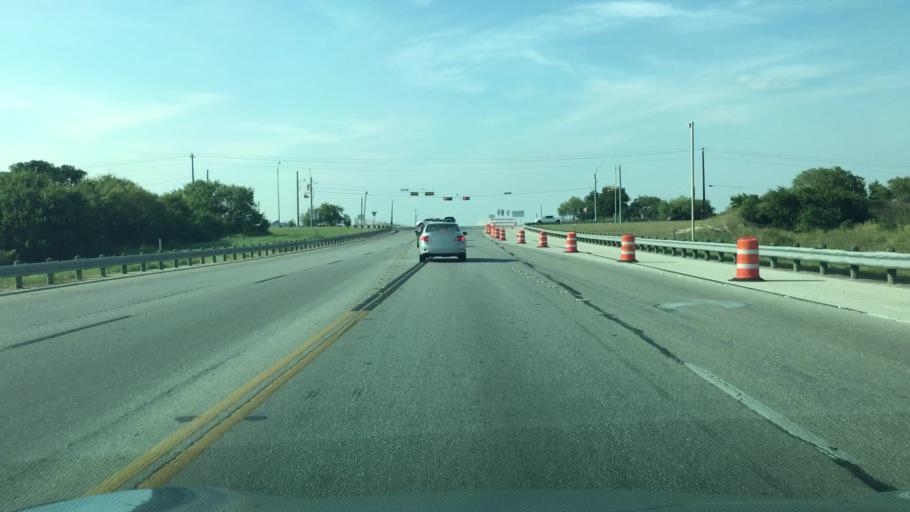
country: US
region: Texas
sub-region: Hays County
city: Buda
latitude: 30.0487
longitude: -97.8748
